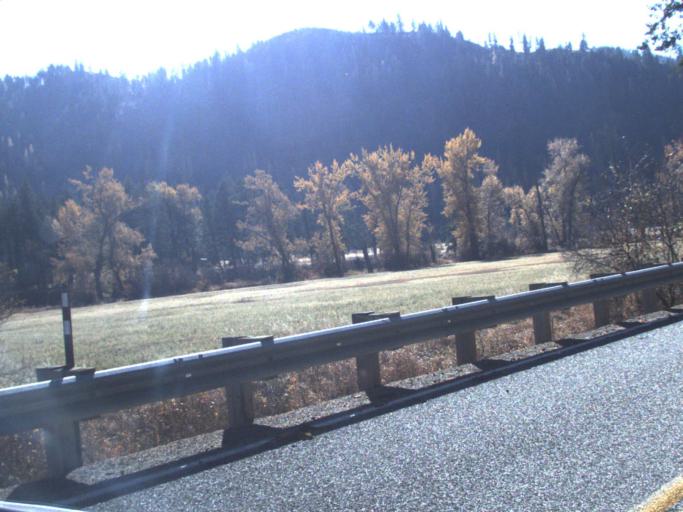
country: CA
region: British Columbia
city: Grand Forks
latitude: 48.9479
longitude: -118.5508
